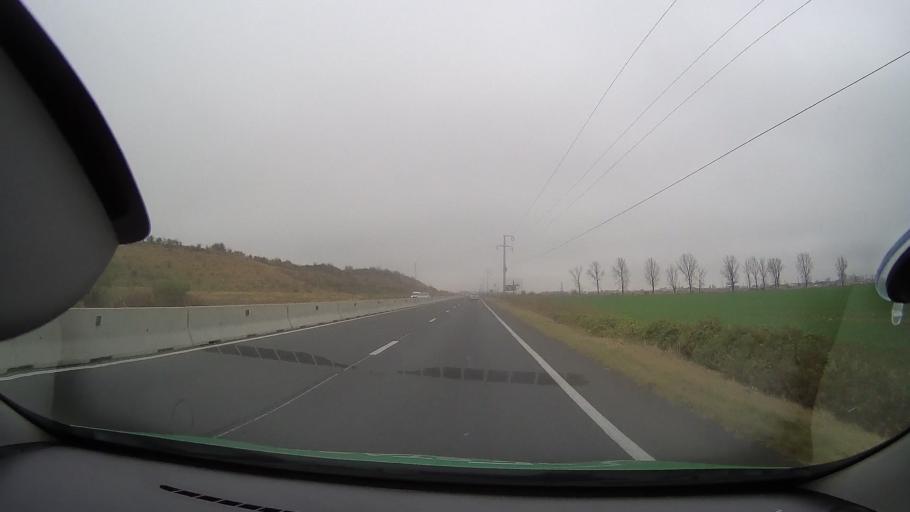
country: RO
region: Prahova
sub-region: Comuna Floresti
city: Floresti
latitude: 45.0468
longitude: 25.8066
